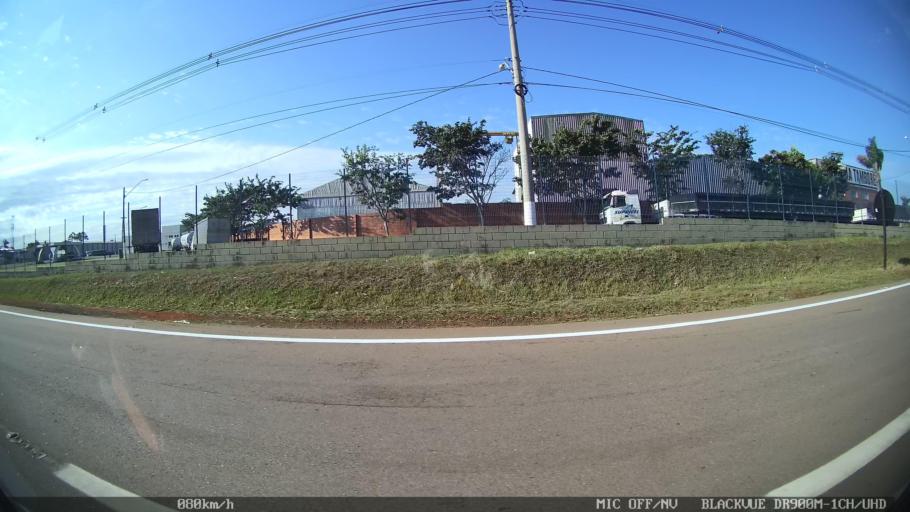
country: BR
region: Sao Paulo
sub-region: Piracicaba
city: Piracicaba
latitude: -22.6664
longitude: -47.6057
